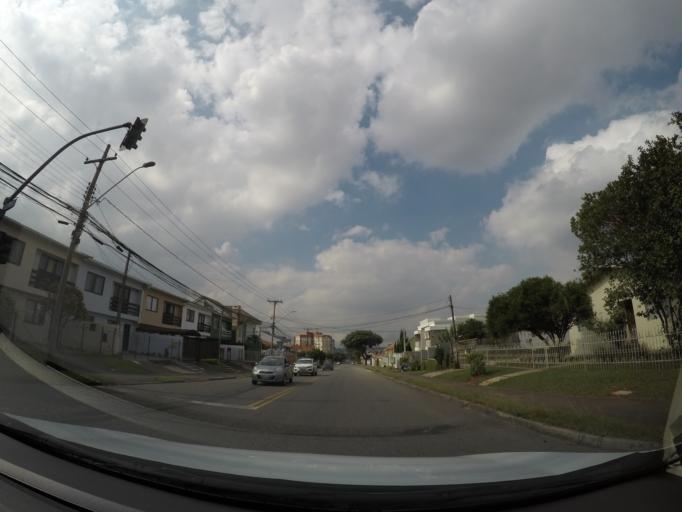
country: BR
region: Parana
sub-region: Curitiba
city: Curitiba
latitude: -25.4871
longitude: -49.2570
